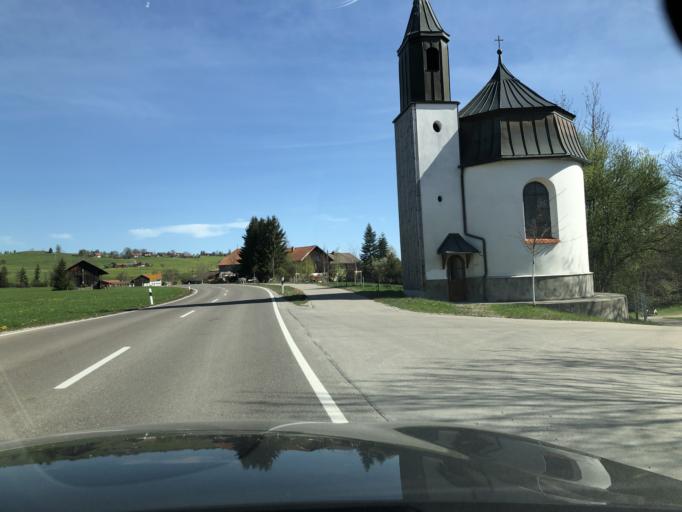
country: DE
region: Bavaria
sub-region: Swabia
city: Seeg
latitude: 47.6349
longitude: 10.6011
